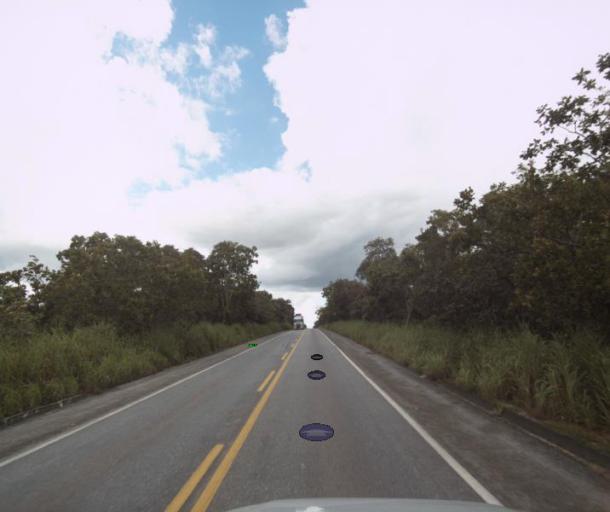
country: BR
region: Goias
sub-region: Porangatu
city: Porangatu
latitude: -13.2770
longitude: -49.1294
